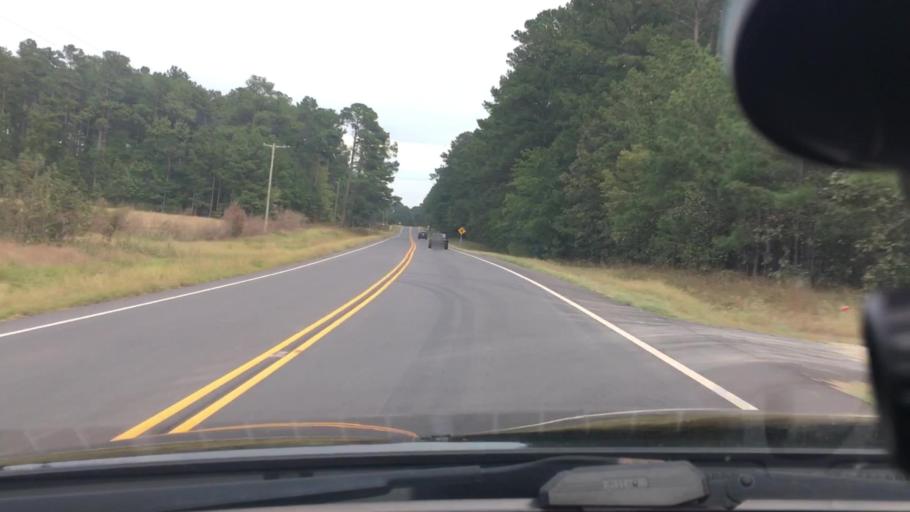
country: US
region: North Carolina
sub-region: Montgomery County
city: Biscoe
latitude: 35.3604
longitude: -79.7504
